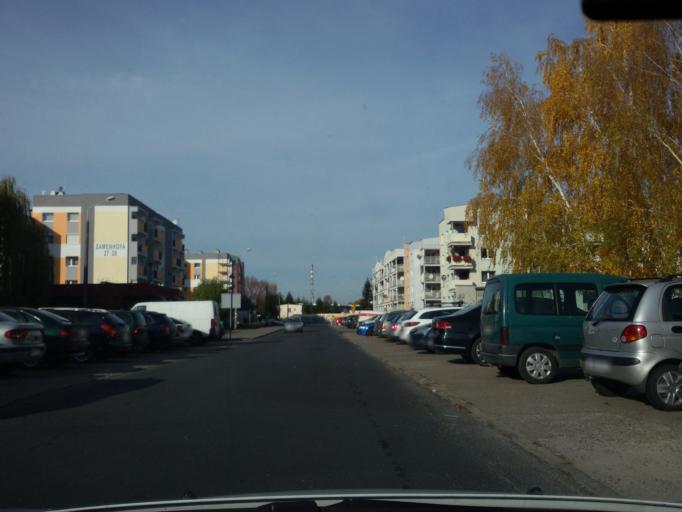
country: PL
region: Greater Poland Voivodeship
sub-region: Leszno
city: Leszno
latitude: 51.8334
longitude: 16.6006
